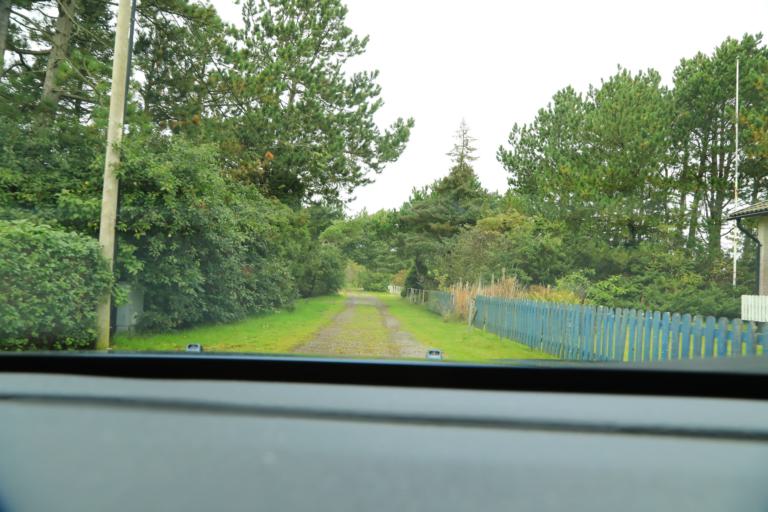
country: SE
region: Halland
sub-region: Varbergs Kommun
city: Tvaaker
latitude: 57.0187
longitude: 12.3415
